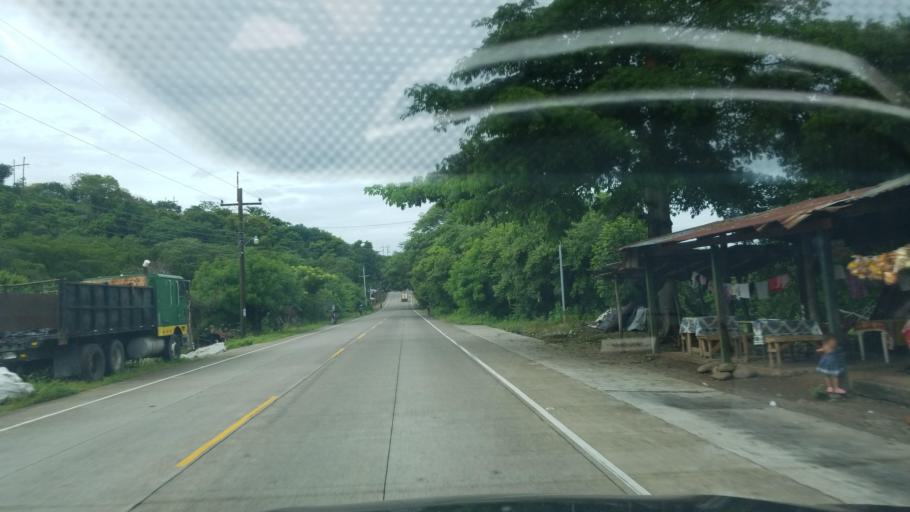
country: HN
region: Choluteca
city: Pespire
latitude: 13.6564
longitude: -87.3649
